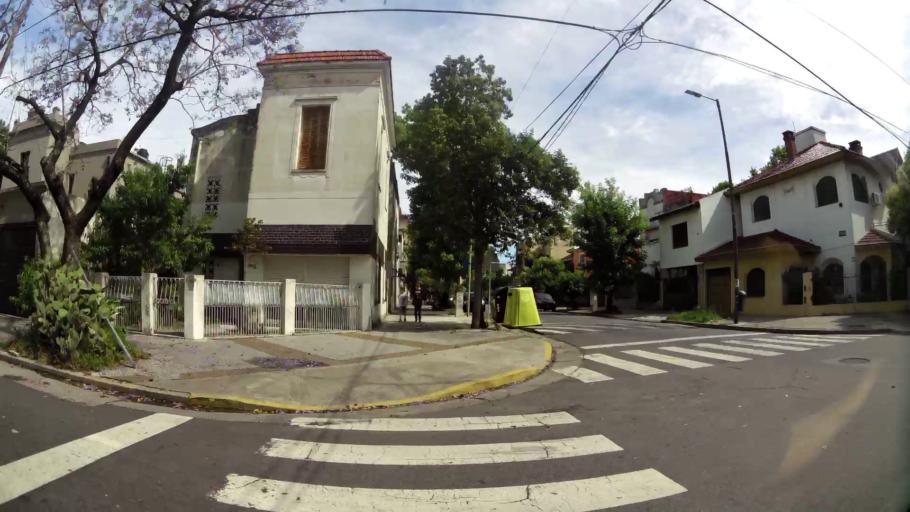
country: AR
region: Buenos Aires
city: San Justo
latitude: -34.6457
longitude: -58.5230
